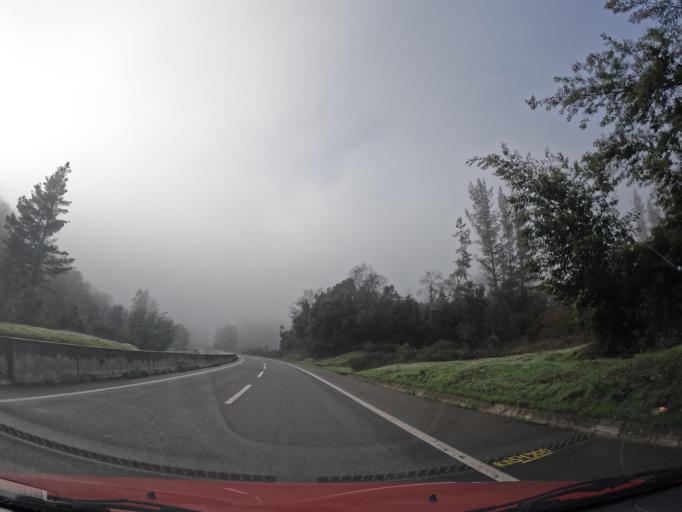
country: CL
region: Biobio
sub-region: Provincia de Concepcion
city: Penco
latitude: -36.7332
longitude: -72.8086
